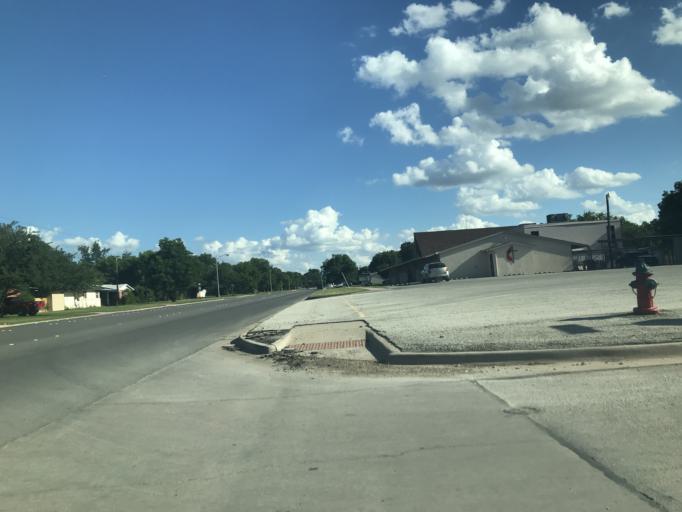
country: US
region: Texas
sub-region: Taylor County
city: Abilene
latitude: 32.4360
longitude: -99.7802
